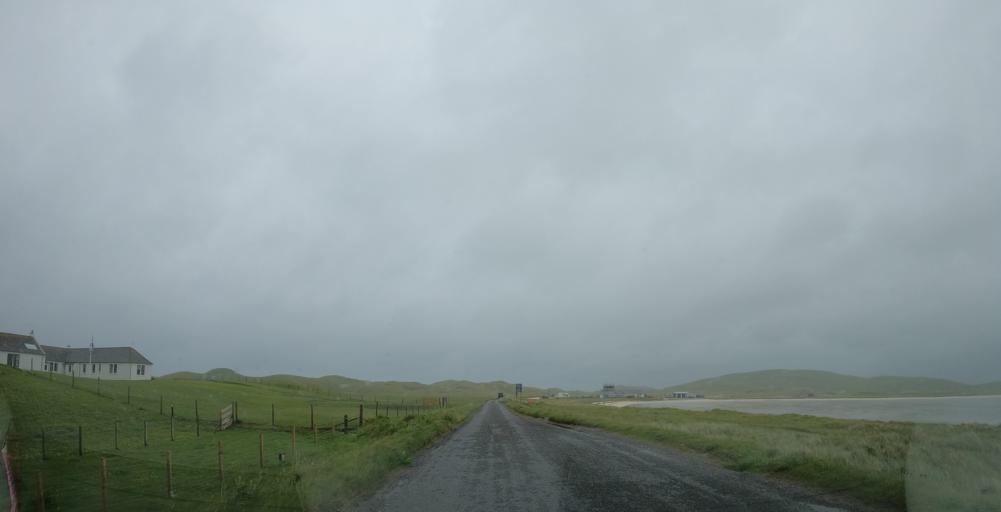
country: GB
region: Scotland
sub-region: Eilean Siar
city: Barra
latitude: 57.0227
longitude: -7.4497
